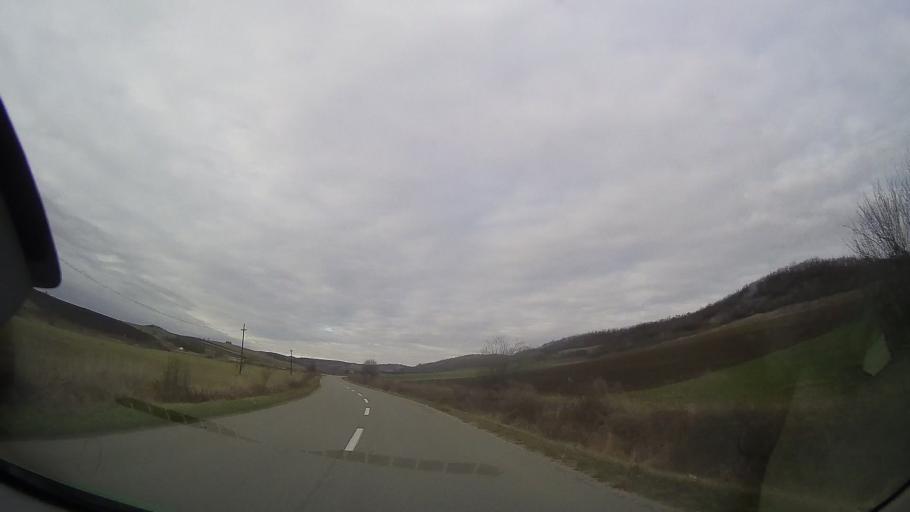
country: RO
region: Bistrita-Nasaud
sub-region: Comuna Milas
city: Milas
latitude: 46.7995
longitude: 24.4219
